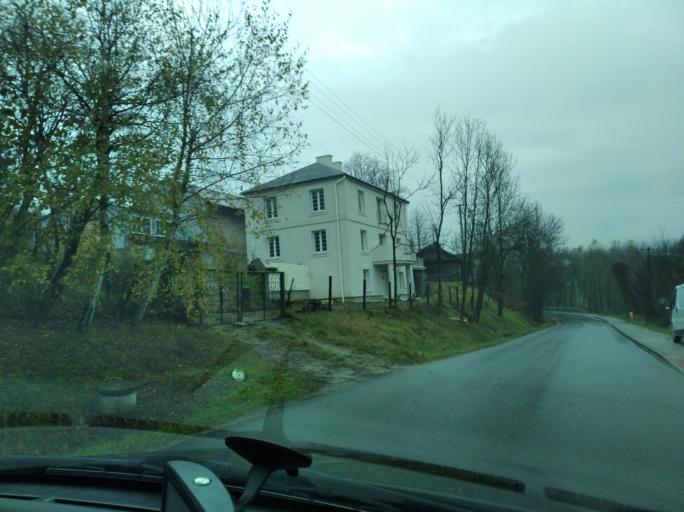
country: PL
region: Subcarpathian Voivodeship
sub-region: Powiat rzeszowski
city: Lubenia
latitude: 49.9290
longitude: 21.9275
